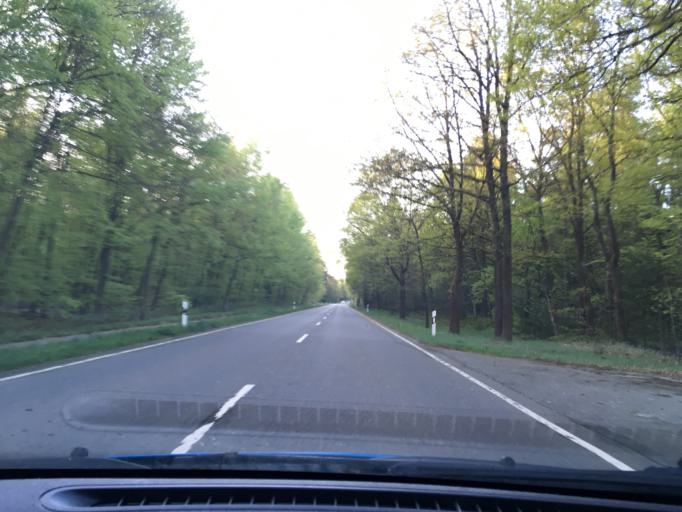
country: DE
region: Lower Saxony
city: Bispingen
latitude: 53.0335
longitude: 9.9985
